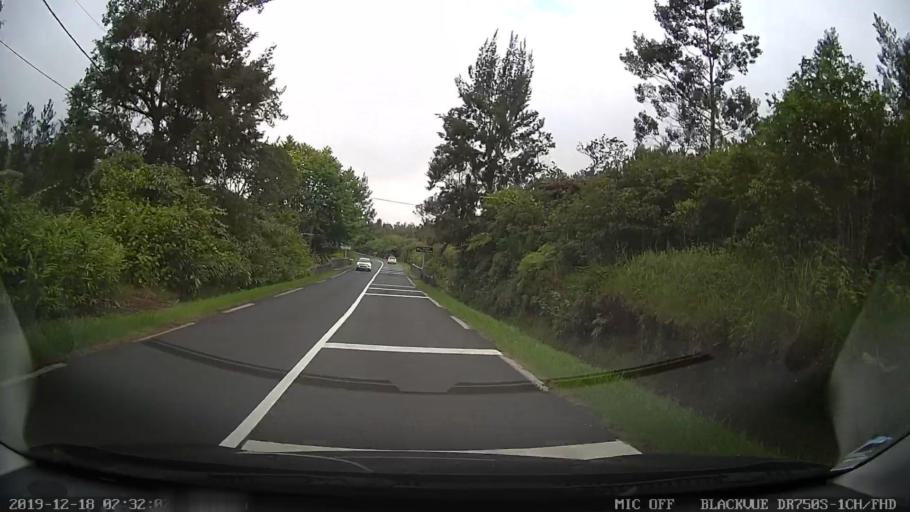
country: RE
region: Reunion
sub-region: Reunion
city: Cilaos
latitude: -21.1571
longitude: 55.6071
